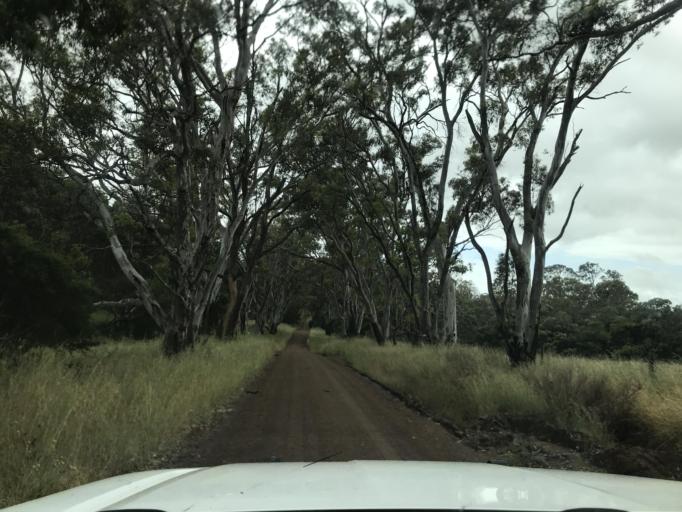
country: AU
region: South Australia
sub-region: Wattle Range
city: Penola
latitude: -37.2345
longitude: 141.4466
